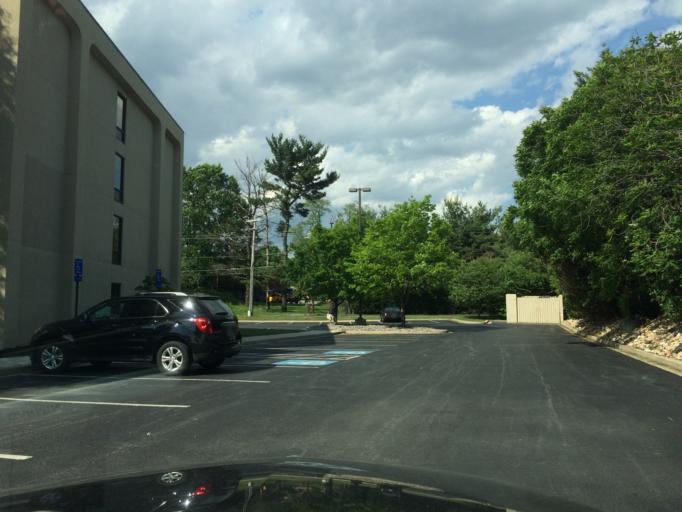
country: US
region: Maryland
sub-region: Washington County
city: Robinwood
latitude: 39.6158
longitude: -77.6902
